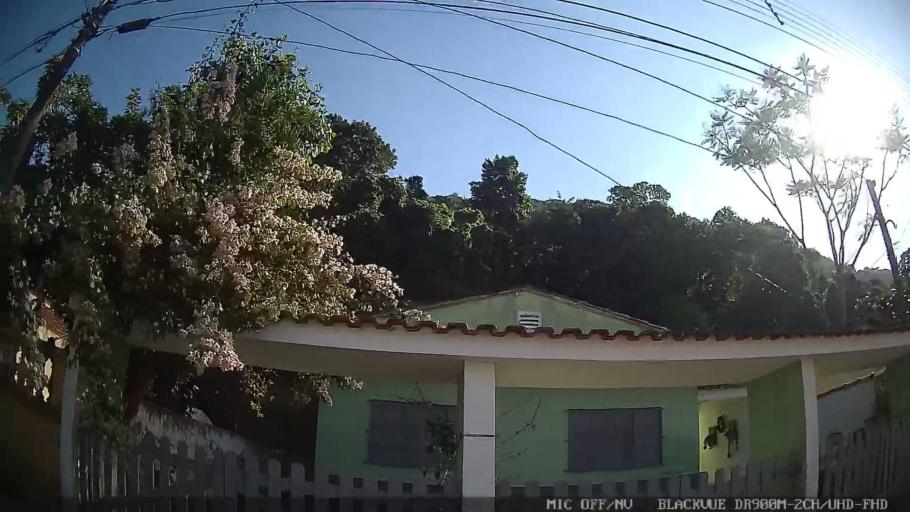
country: BR
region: Sao Paulo
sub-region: Guaruja
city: Guaruja
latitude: -24.0129
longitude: -46.2859
